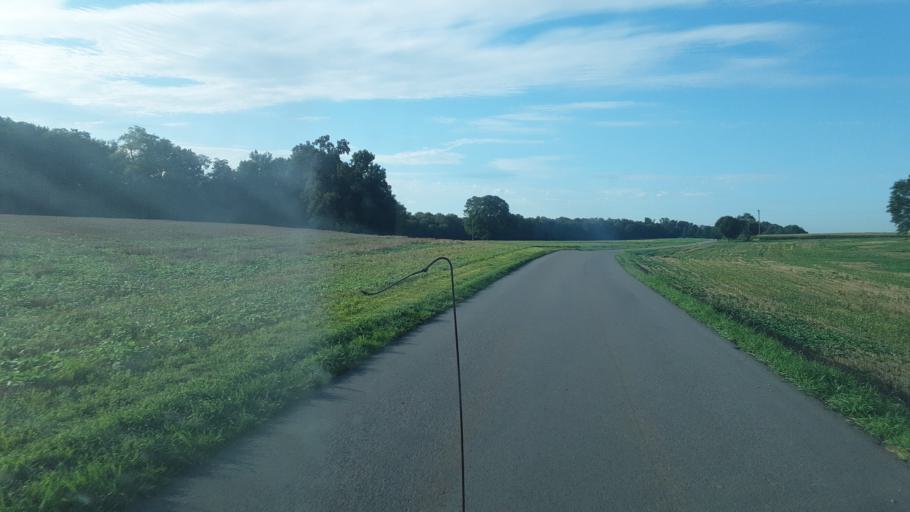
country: US
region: Kentucky
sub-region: Todd County
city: Guthrie
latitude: 36.7091
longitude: -87.1704
